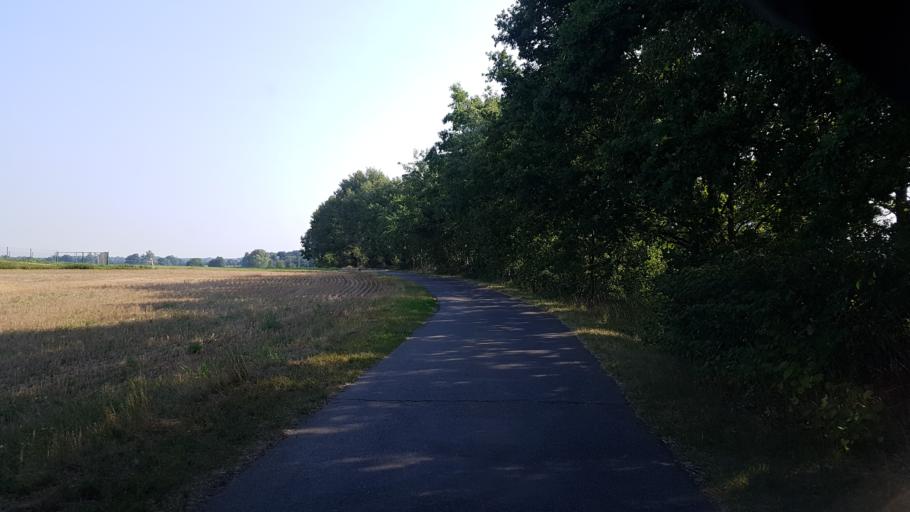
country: DE
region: Brandenburg
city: Drebkau
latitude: 51.6689
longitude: 14.2406
